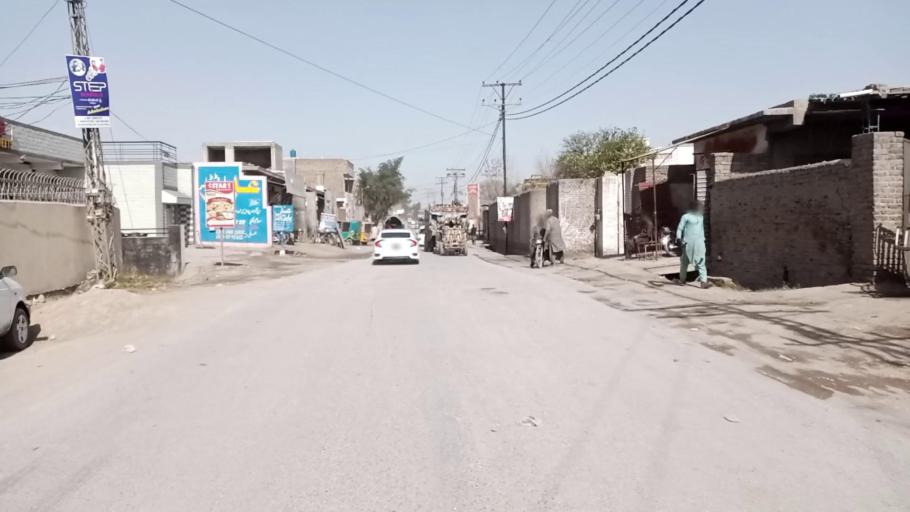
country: PK
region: Khyber Pakhtunkhwa
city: Peshawar
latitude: 34.0129
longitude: 71.6471
